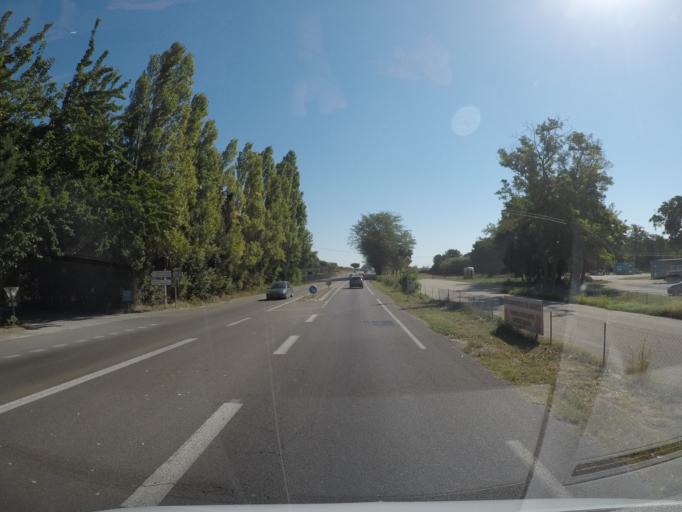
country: FR
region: Languedoc-Roussillon
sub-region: Departement du Gard
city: Uzes
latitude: 43.9911
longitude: 4.4324
